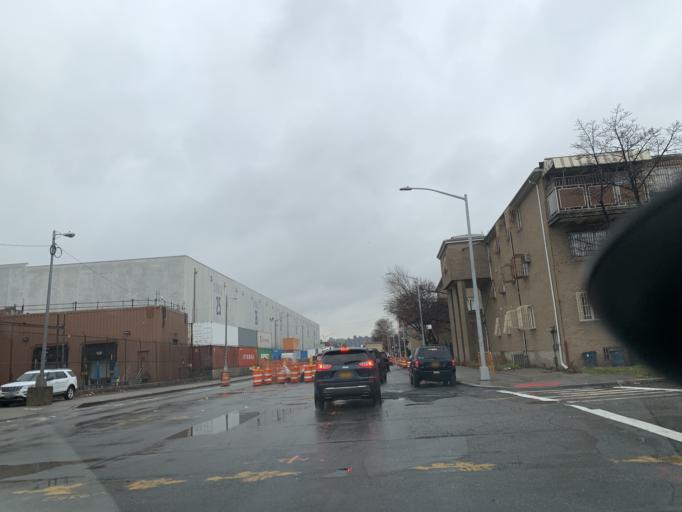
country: US
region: New York
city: New York City
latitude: 40.7015
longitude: -73.9637
